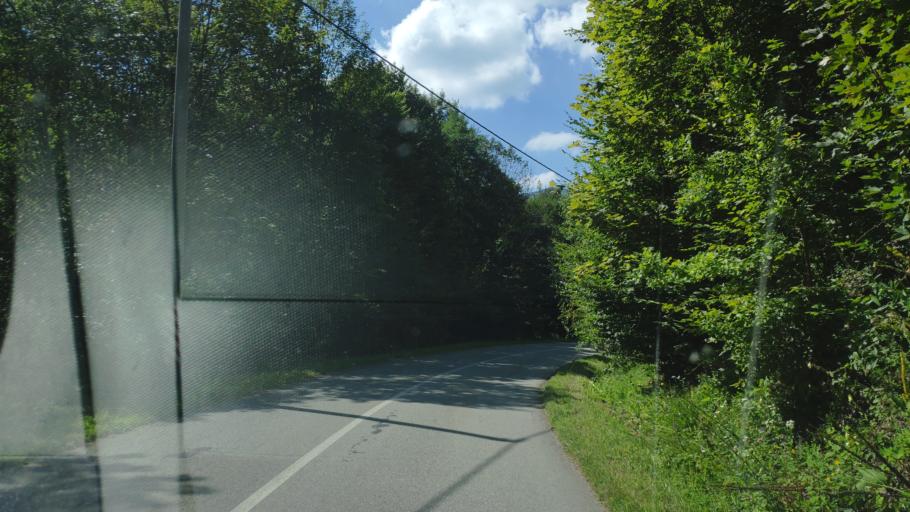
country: PL
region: Subcarpathian Voivodeship
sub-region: Powiat leski
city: Cisna
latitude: 49.0735
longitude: 22.3767
